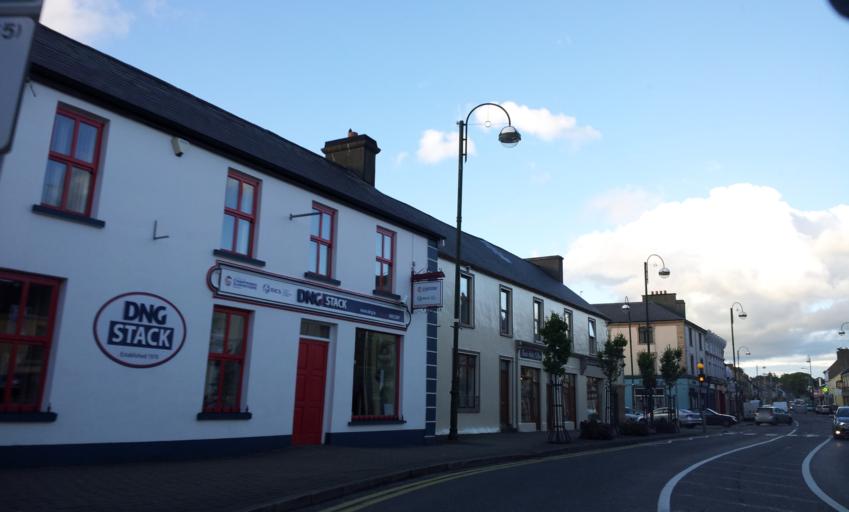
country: IE
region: Munster
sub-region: County Limerick
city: Abbeyfeale
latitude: 52.3848
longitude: -9.3018
